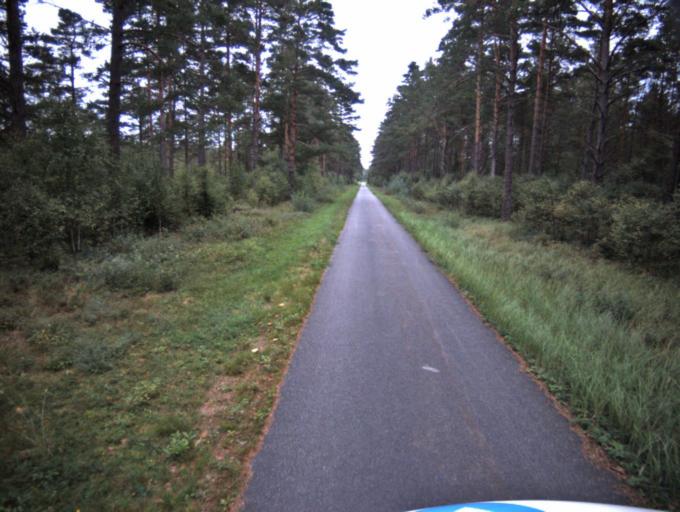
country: SE
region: Vaestra Goetaland
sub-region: Ulricehamns Kommun
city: Ulricehamn
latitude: 57.9464
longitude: 13.5011
